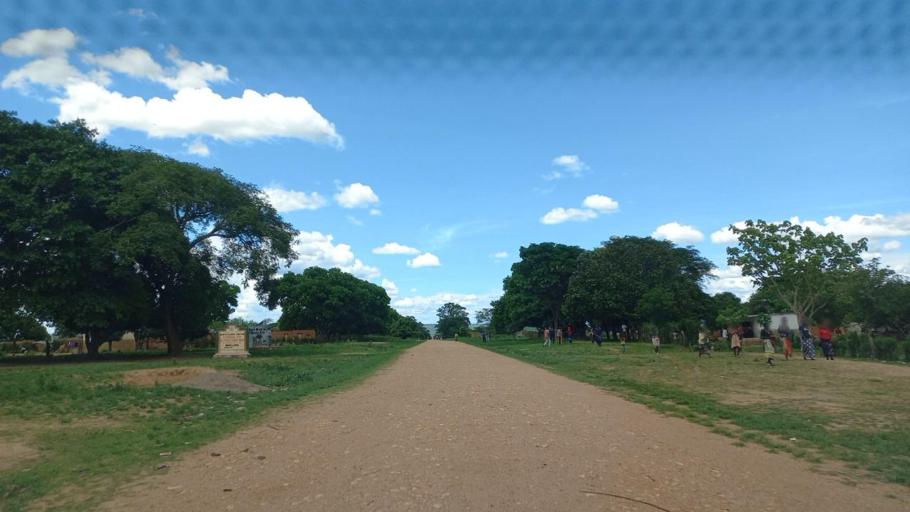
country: ZM
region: North-Western
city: Mwinilunga
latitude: -12.3046
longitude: 24.2623
